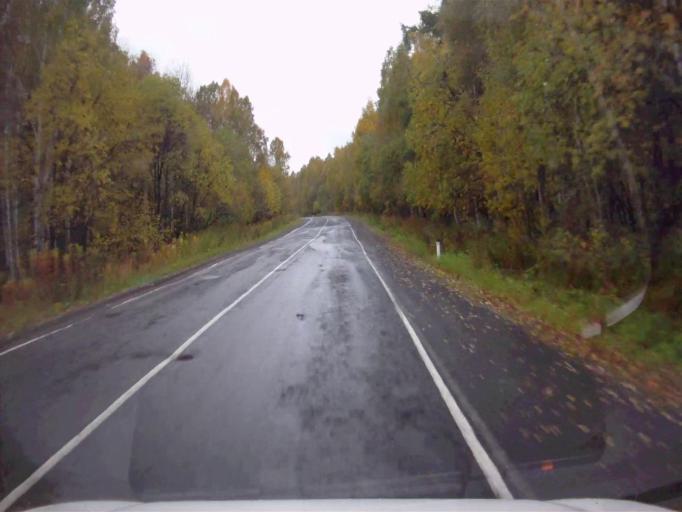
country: RU
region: Chelyabinsk
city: Nizhniy Ufaley
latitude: 56.0546
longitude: 60.0536
